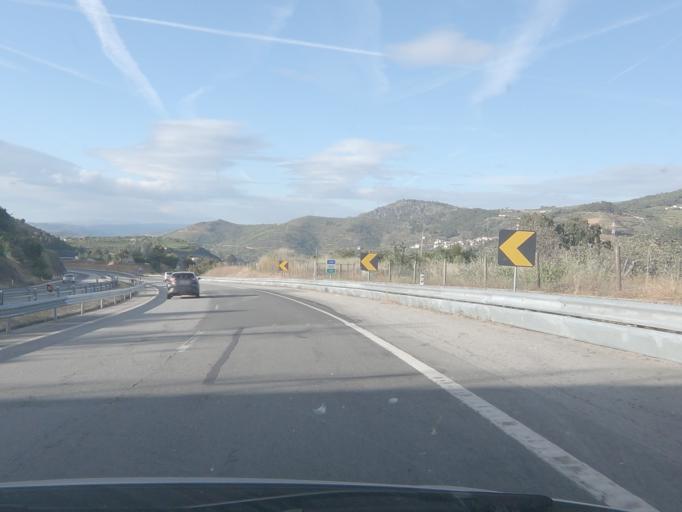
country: PT
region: Viseu
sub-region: Lamego
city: Lamego
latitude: 41.0896
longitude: -7.7840
